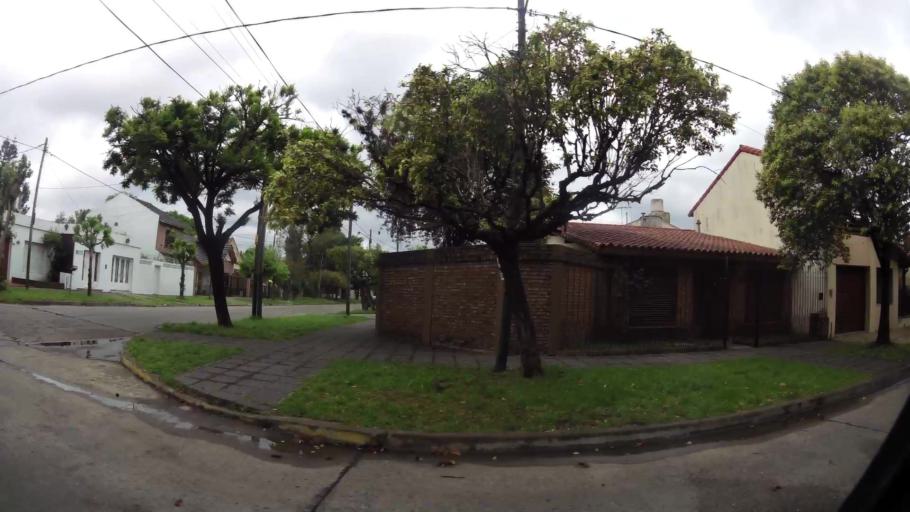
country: AR
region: Buenos Aires
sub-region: Partido de Lomas de Zamora
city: Lomas de Zamora
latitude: -34.7467
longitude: -58.3795
